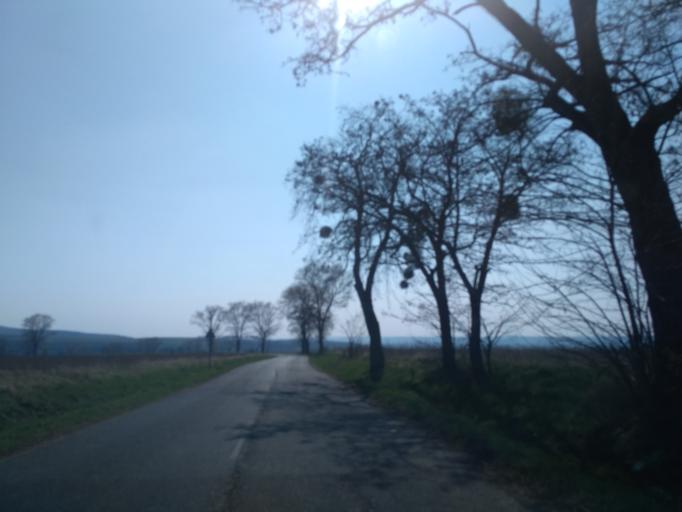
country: HU
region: Borsod-Abauj-Zemplen
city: Gonc
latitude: 48.5393
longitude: 21.3375
